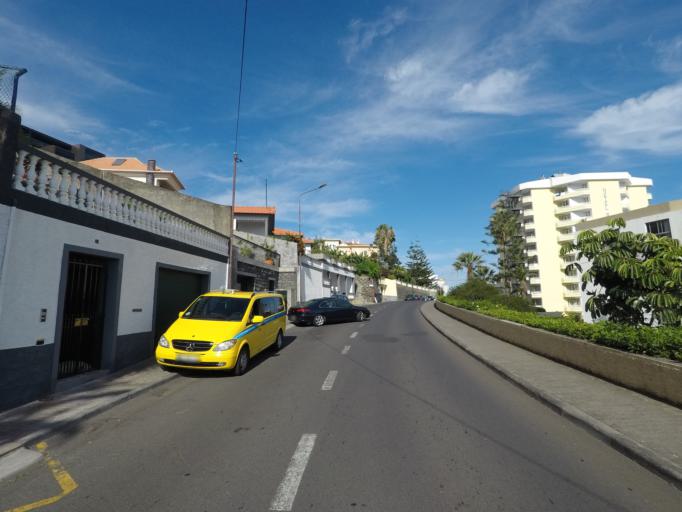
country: PT
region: Madeira
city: Camara de Lobos
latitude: 32.6392
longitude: -16.9336
